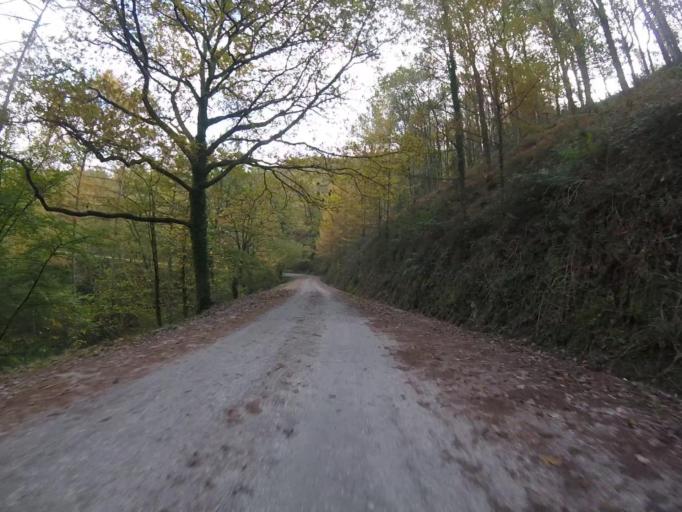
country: ES
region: Navarre
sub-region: Provincia de Navarra
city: Goizueta
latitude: 43.2185
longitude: -1.8478
